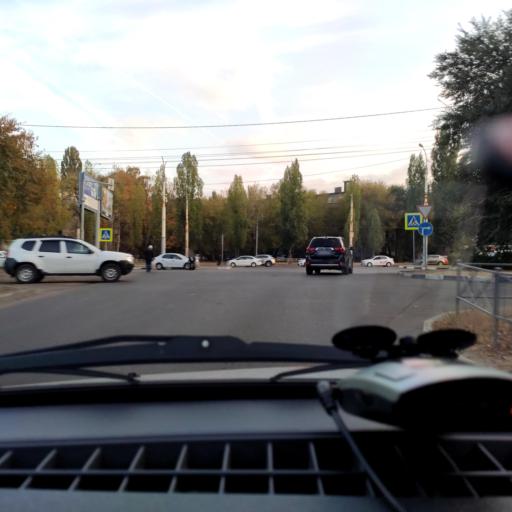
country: RU
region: Voronezj
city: Voronezh
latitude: 51.6562
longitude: 39.1389
